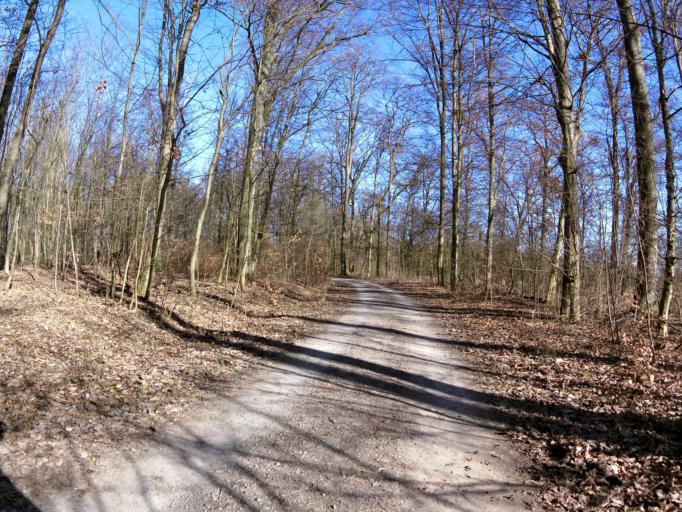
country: DE
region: Bavaria
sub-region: Regierungsbezirk Unterfranken
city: Estenfeld
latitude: 49.8528
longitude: 9.9963
